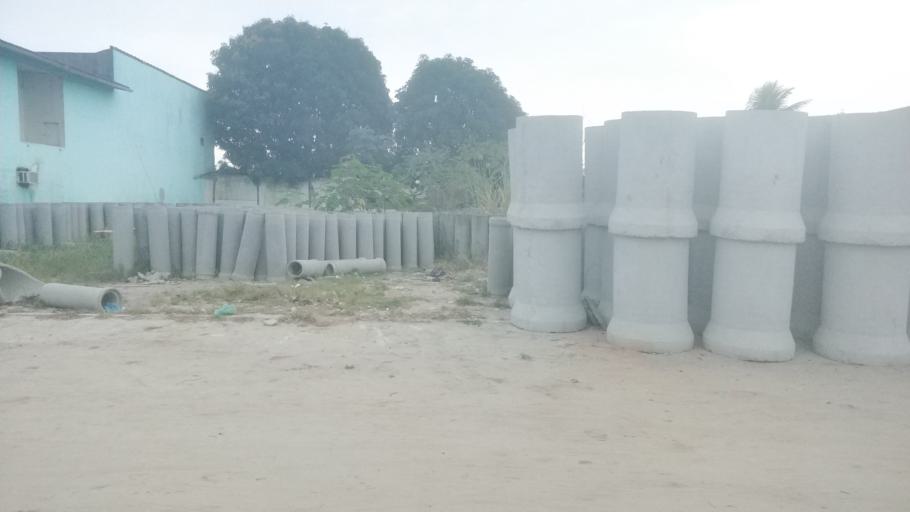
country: BR
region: Rio de Janeiro
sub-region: Seropedica
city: Seropedica
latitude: -22.8058
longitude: -43.6376
